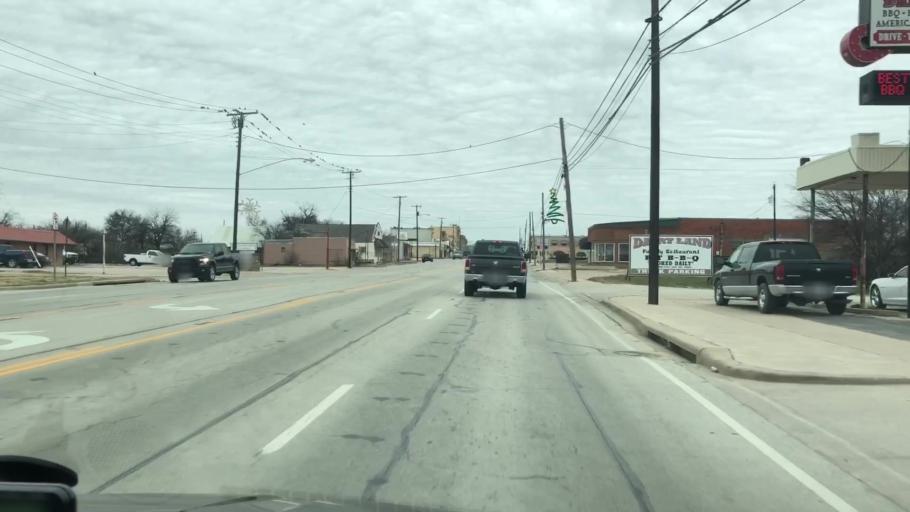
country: US
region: Texas
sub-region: Jack County
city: Jacksboro
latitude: 33.2149
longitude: -98.1588
